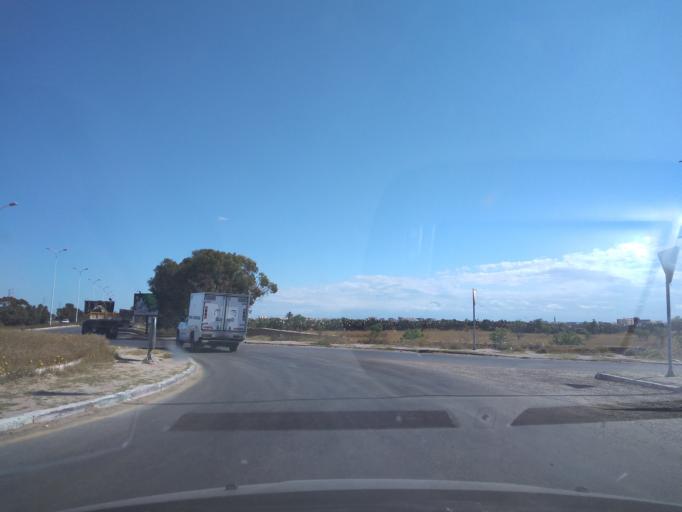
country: TN
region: Safaqis
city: Sfax
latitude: 34.8309
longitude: 10.7255
